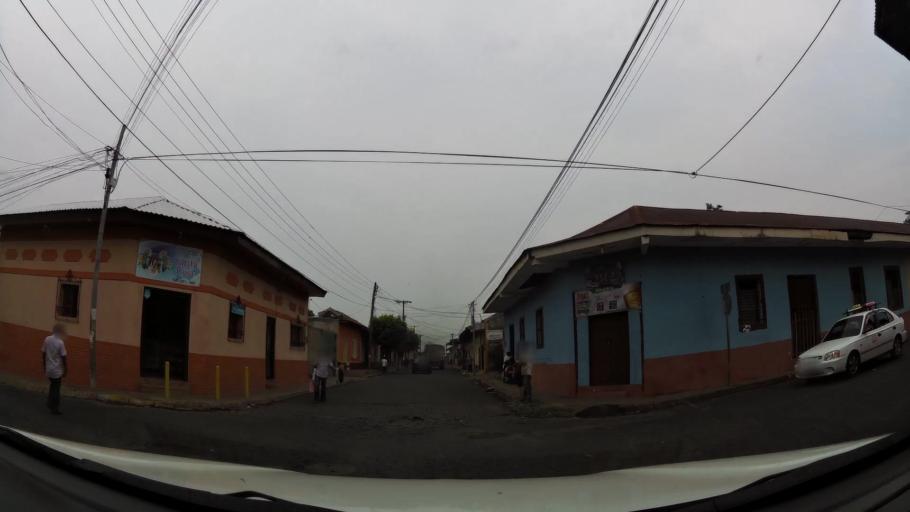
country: NI
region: Leon
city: Leon
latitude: 12.4361
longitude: -86.8865
